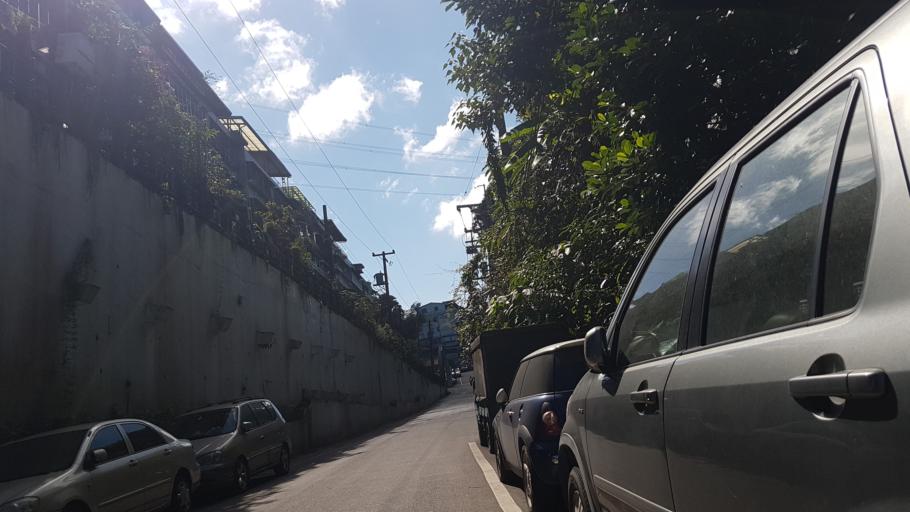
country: TW
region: Taipei
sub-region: Taipei
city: Banqiao
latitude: 24.9503
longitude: 121.5303
